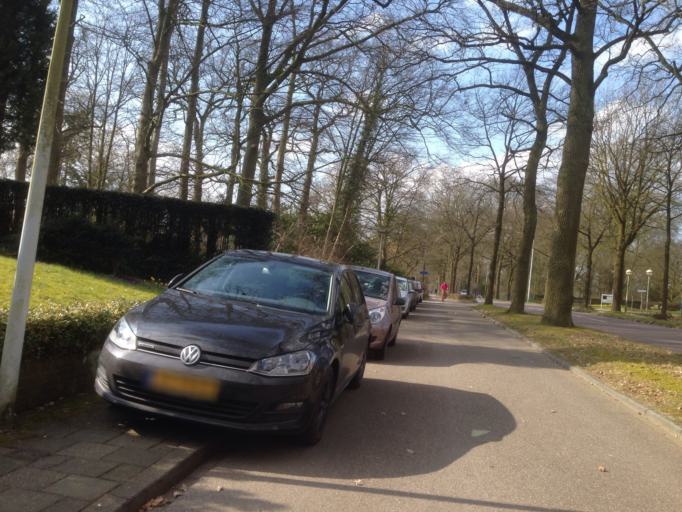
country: NL
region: Gelderland
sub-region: Gemeente Wageningen
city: Wageningen
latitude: 51.9668
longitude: 5.6814
